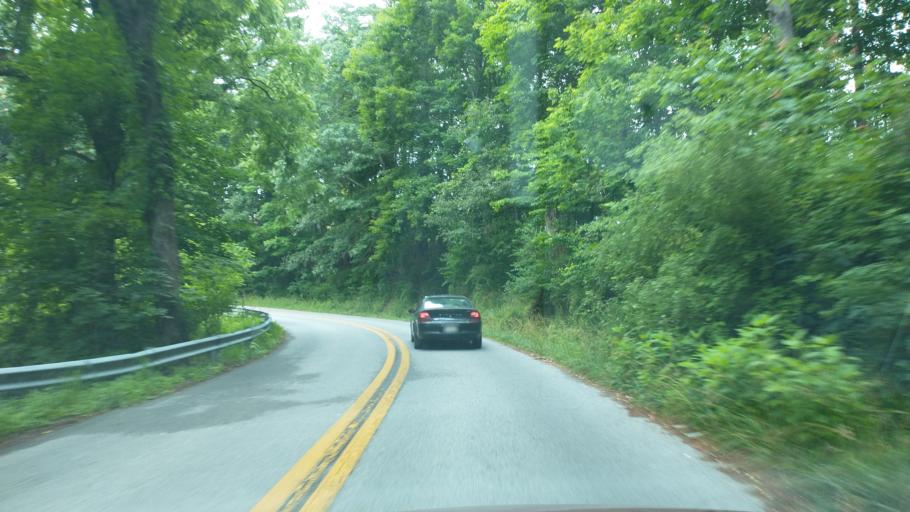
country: US
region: West Virginia
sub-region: Mercer County
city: Athens
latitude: 37.4229
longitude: -81.0052
